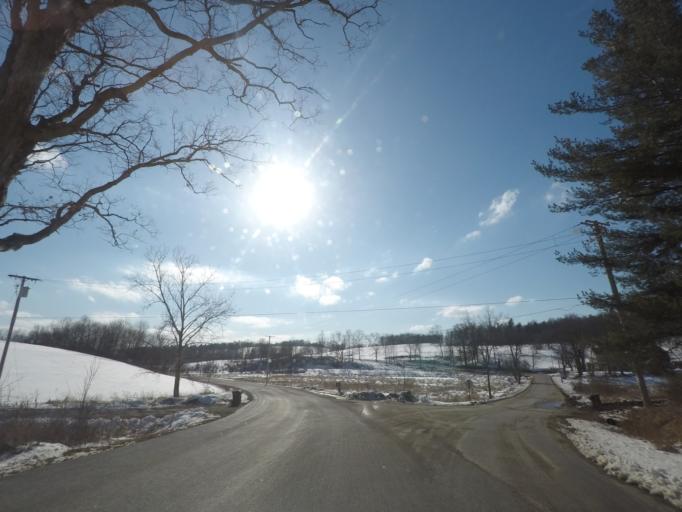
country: US
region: New York
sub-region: Rensselaer County
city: Hoosick Falls
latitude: 42.8831
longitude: -73.4973
